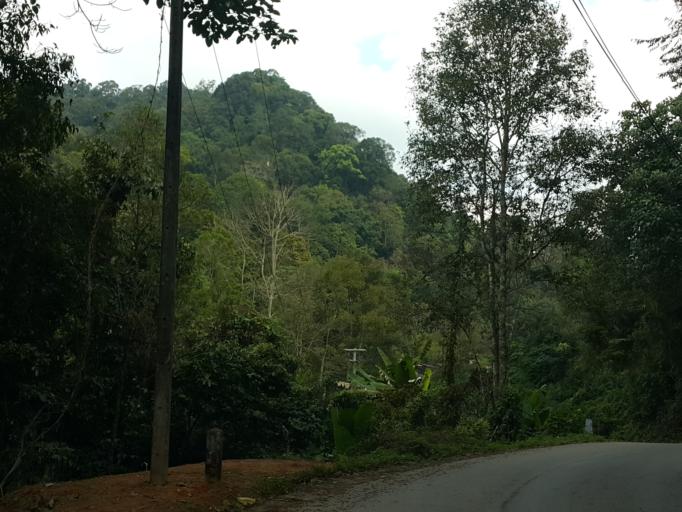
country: TH
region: Chiang Mai
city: Mae On
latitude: 18.8651
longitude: 99.3475
